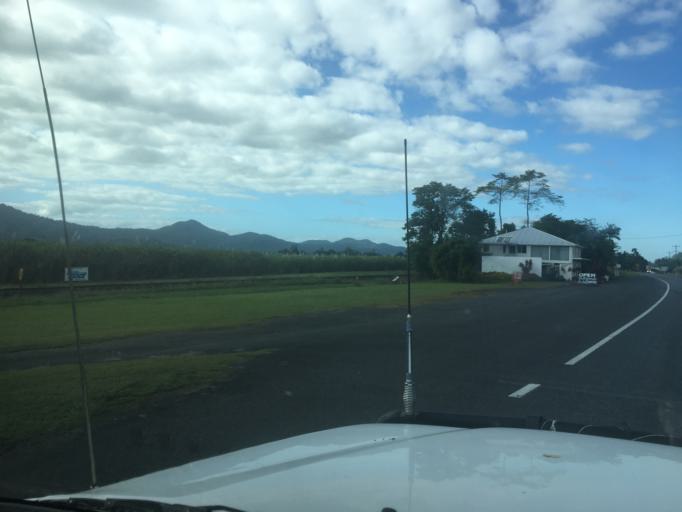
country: AU
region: Queensland
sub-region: Cassowary Coast
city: Innisfail
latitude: -17.2729
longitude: 145.9203
